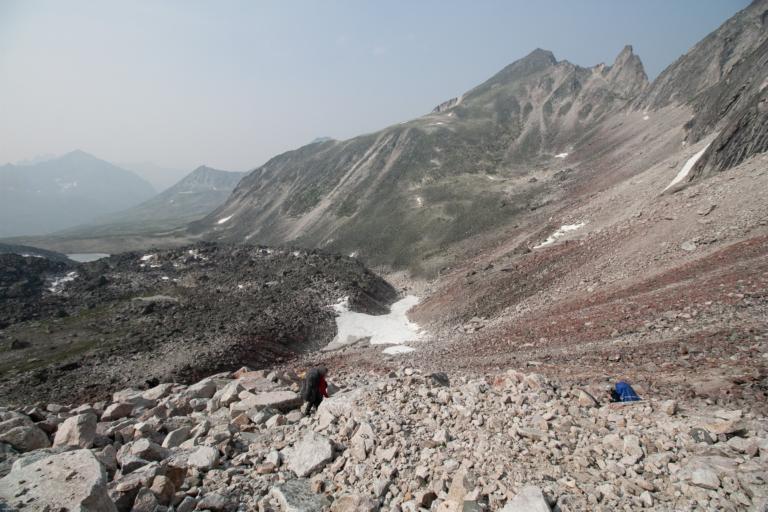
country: RU
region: Respublika Buryatiya
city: Novyy Uoyan
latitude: 56.2183
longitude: 110.9991
